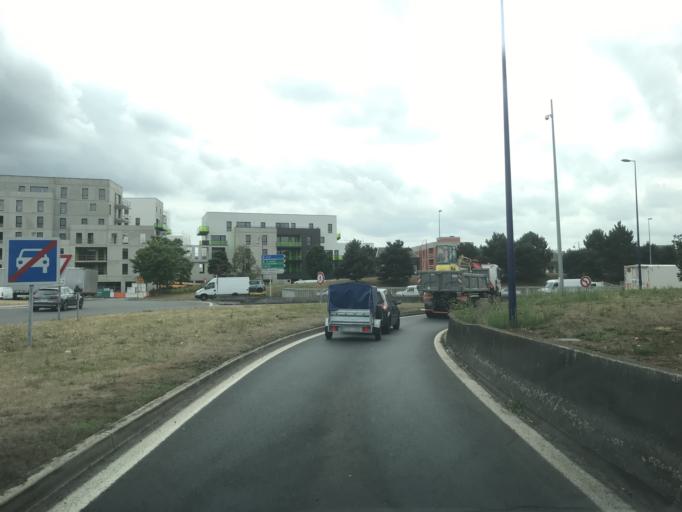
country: FR
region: Haute-Normandie
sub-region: Departement de la Seine-Maritime
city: Le Petit-Quevilly
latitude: 49.4354
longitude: 1.0714
